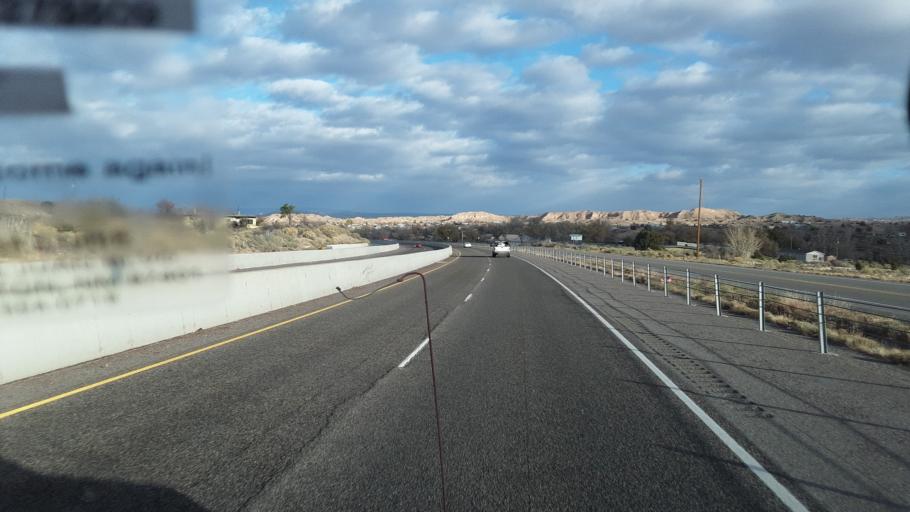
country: US
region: New Mexico
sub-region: Santa Fe County
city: El Valle de Arroyo Seco
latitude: 35.9541
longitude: -106.0206
